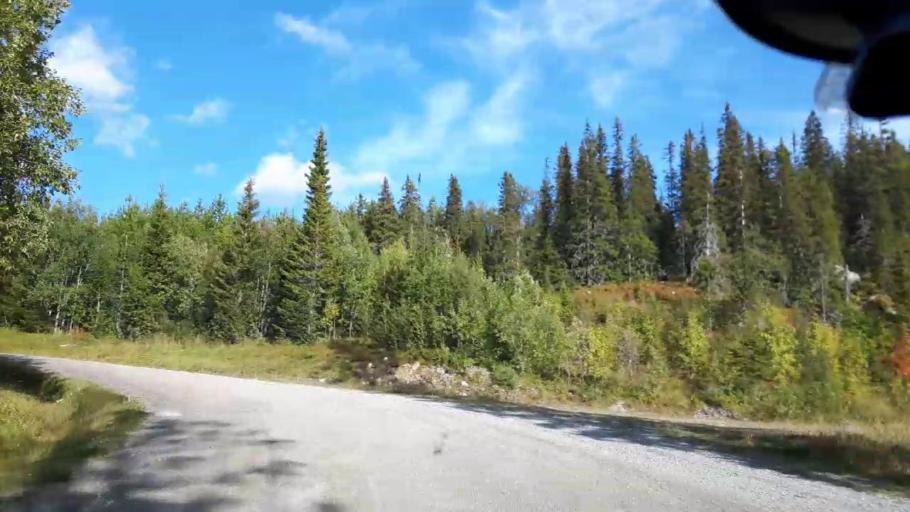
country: SE
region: Jaemtland
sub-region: Ragunda Kommun
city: Hammarstrand
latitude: 63.4108
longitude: 16.0921
